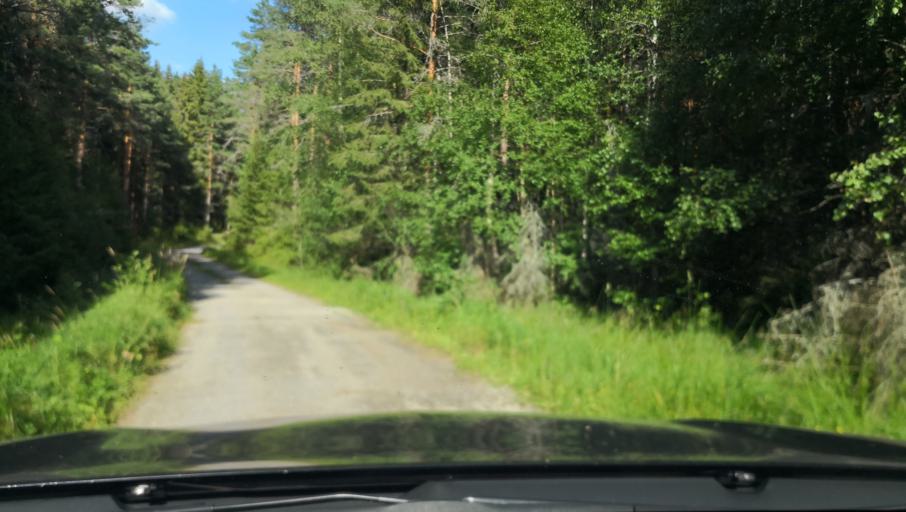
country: SE
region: Vaestmanland
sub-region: Vasteras
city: Skultuna
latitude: 59.7238
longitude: 16.3395
